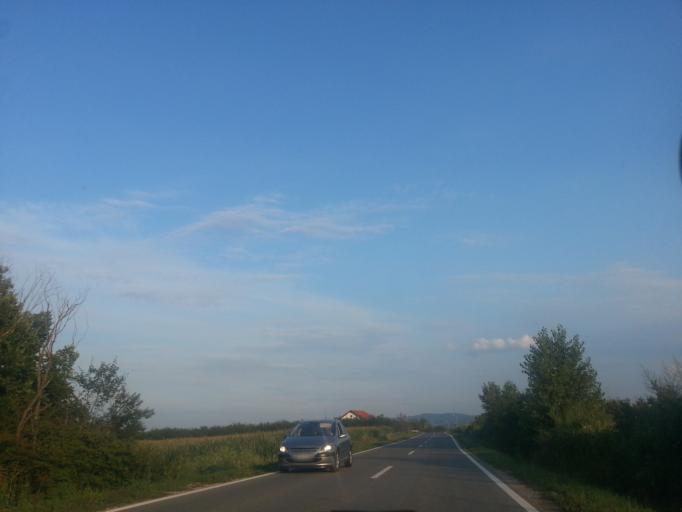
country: BA
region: Brcko
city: Brcko
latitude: 44.7676
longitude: 18.8125
